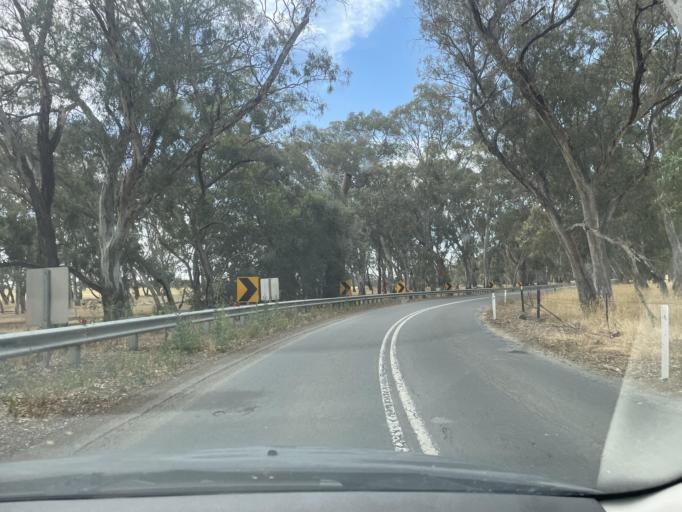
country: AU
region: South Australia
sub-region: Clare and Gilbert Valleys
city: Clare
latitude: -33.9020
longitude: 138.6453
